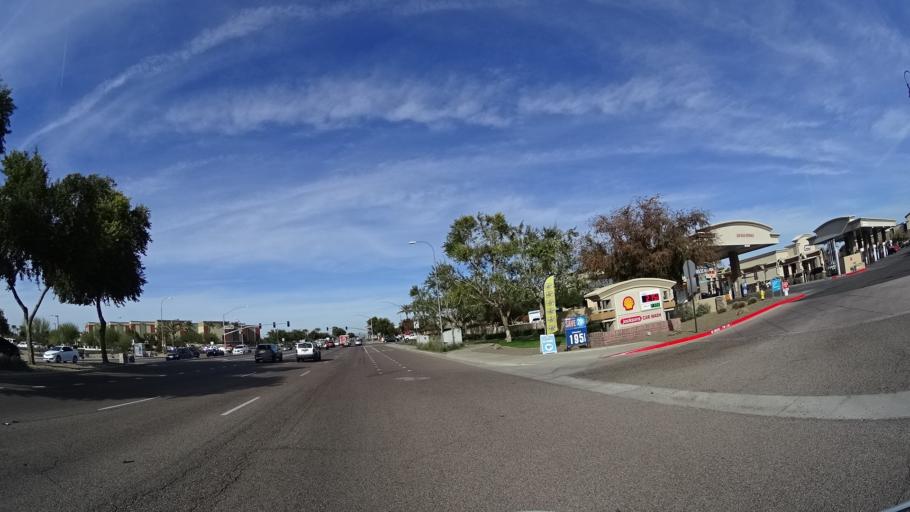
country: US
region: Arizona
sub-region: Maricopa County
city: Chandler
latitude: 33.2762
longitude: -111.7895
